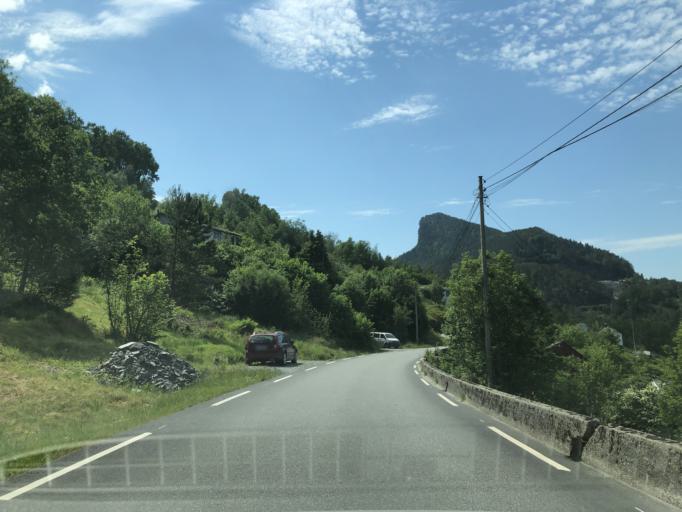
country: NO
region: Hordaland
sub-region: Jondal
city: Jondal
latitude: 60.3055
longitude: 6.2936
